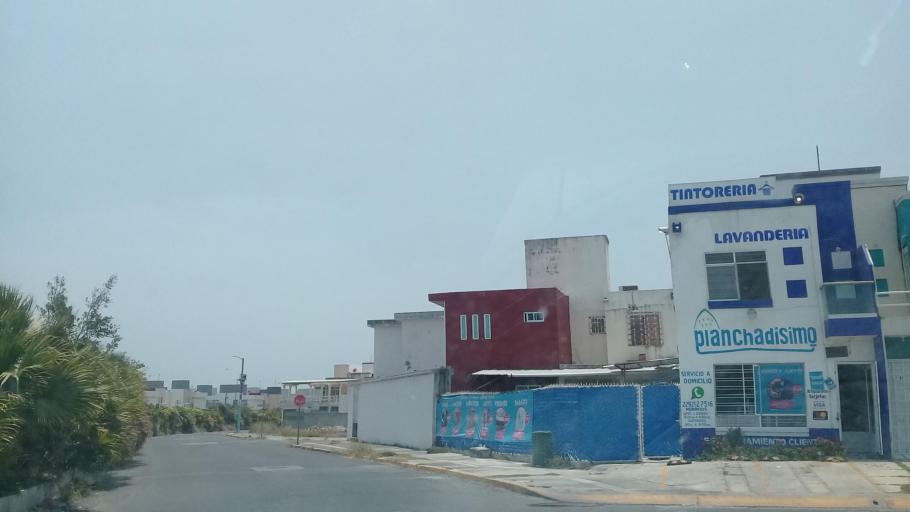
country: MX
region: Veracruz
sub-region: Veracruz
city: Hacienda Sotavento
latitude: 19.1330
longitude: -96.1743
